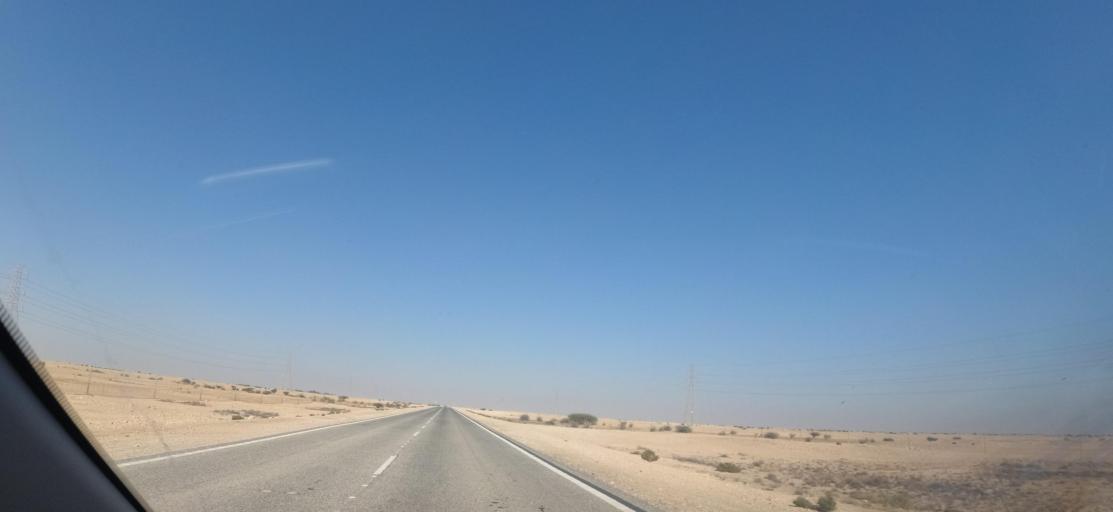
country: QA
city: Al Jumayliyah
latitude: 25.6523
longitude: 51.1130
